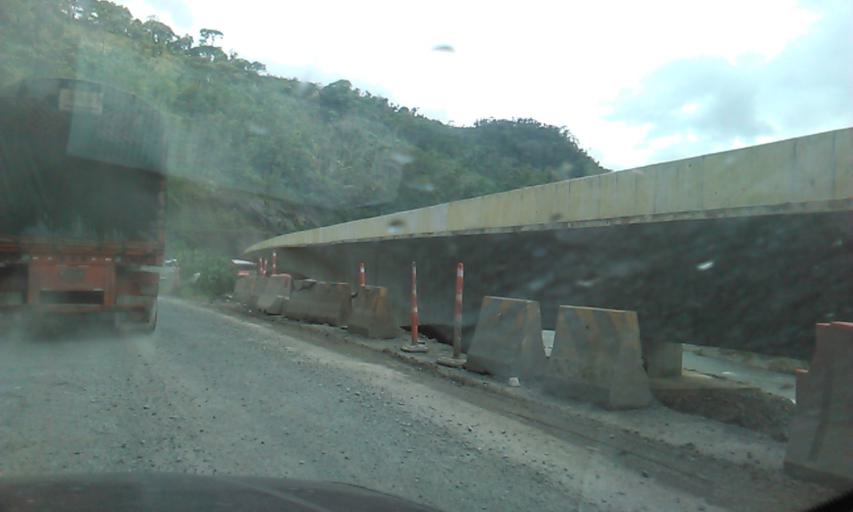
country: CO
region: Valle del Cauca
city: Dagua
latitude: 3.8356
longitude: -76.7907
